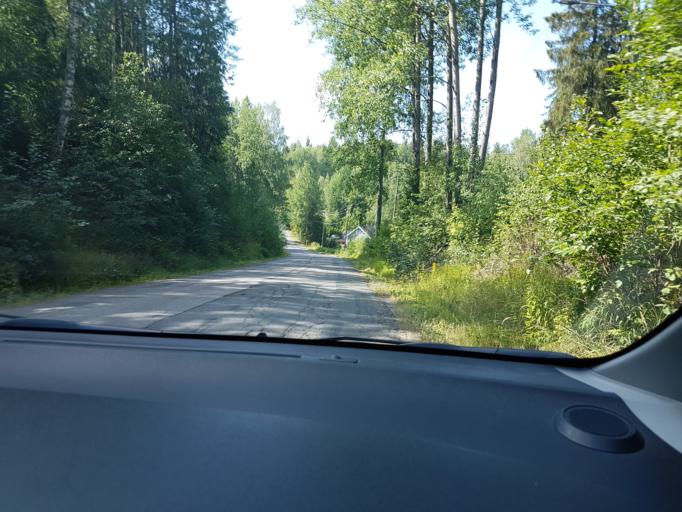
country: FI
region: Uusimaa
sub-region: Helsinki
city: Kilo
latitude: 60.3315
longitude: 24.7748
